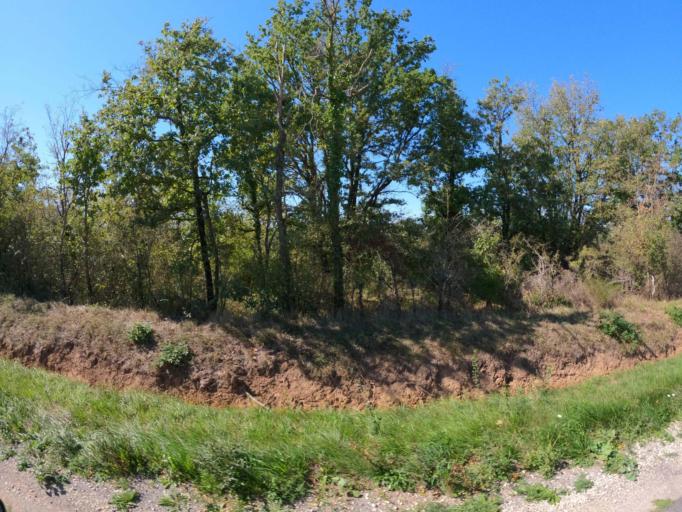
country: FR
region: Poitou-Charentes
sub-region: Departement de la Vienne
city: Lathus-Saint-Remy
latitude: 46.3600
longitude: 0.9429
